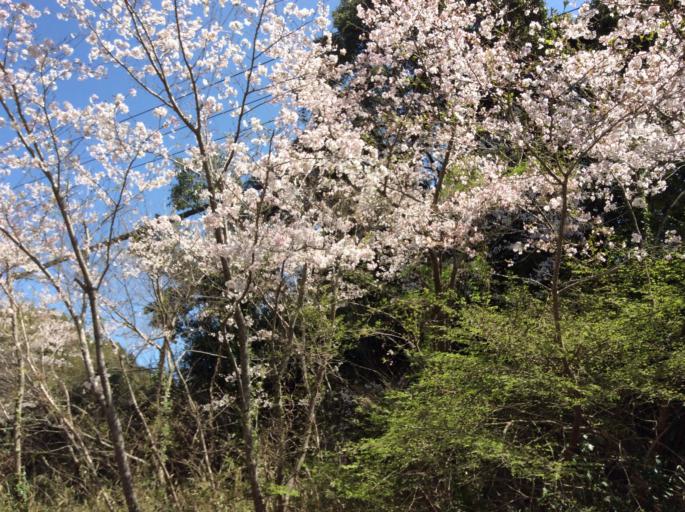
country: JP
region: Shizuoka
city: Kanaya
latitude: 34.7857
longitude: 138.1176
